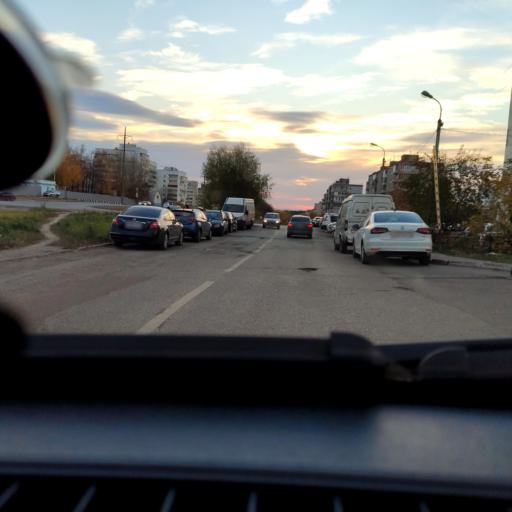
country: RU
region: Bashkortostan
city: Ufa
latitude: 54.7042
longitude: 55.9909
